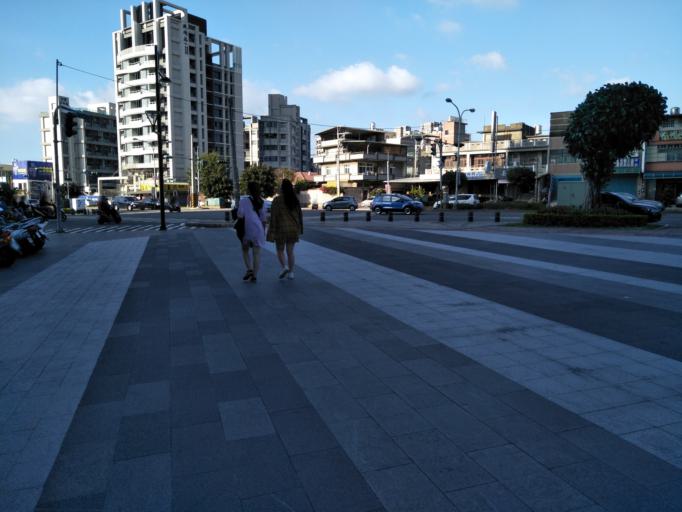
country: TW
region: Taiwan
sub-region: Hsinchu
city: Hsinchu
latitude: 24.6893
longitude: 120.9045
